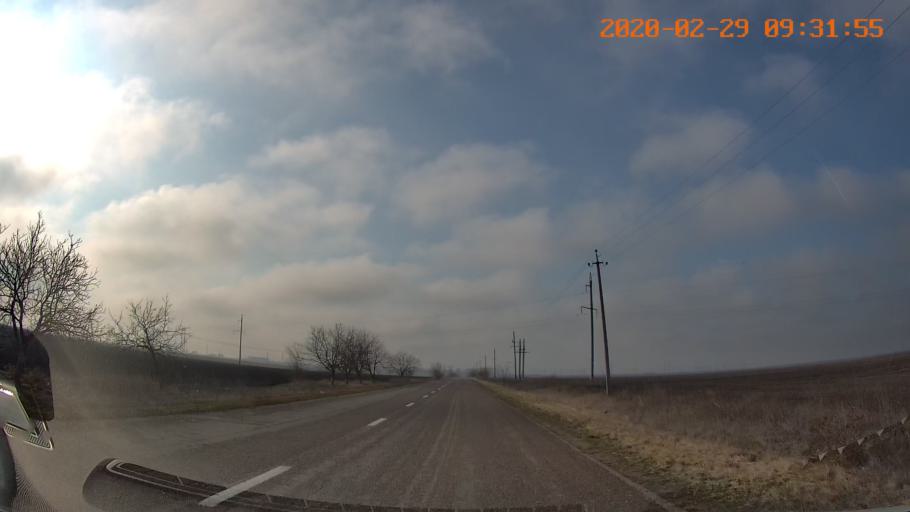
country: MD
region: Telenesti
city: Dnestrovsc
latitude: 46.6464
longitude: 29.9087
